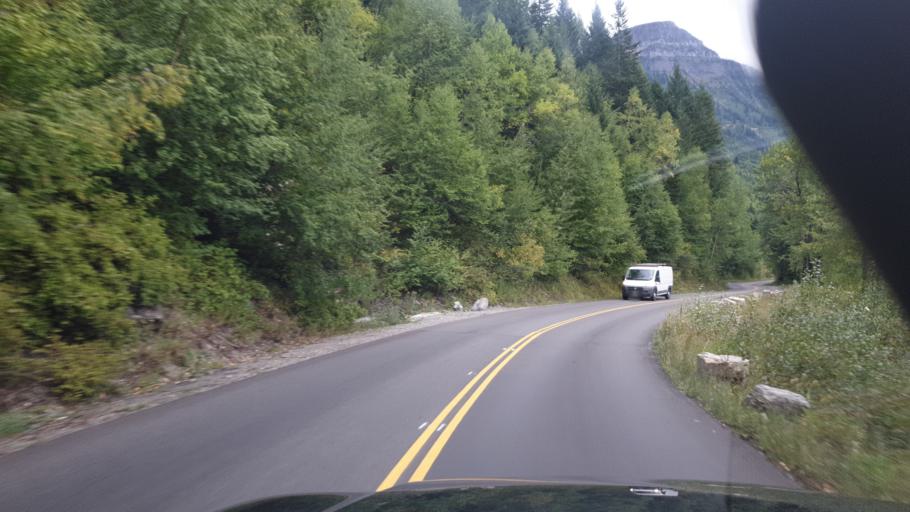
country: US
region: Montana
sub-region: Flathead County
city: Columbia Falls
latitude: 48.7476
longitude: -113.7782
